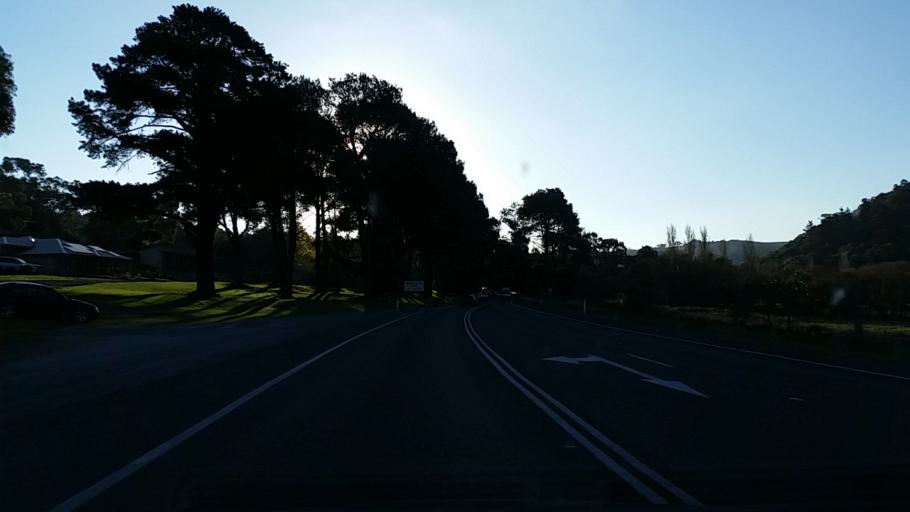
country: AU
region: South Australia
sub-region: Alexandrina
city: Mount Compass
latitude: -35.3458
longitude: 138.6169
